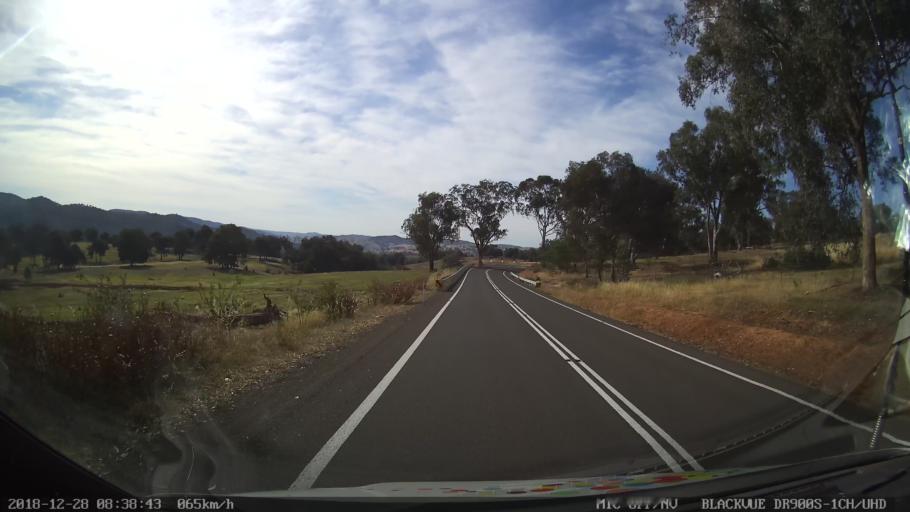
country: AU
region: New South Wales
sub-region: Blayney
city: Blayney
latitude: -34.0062
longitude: 149.3161
